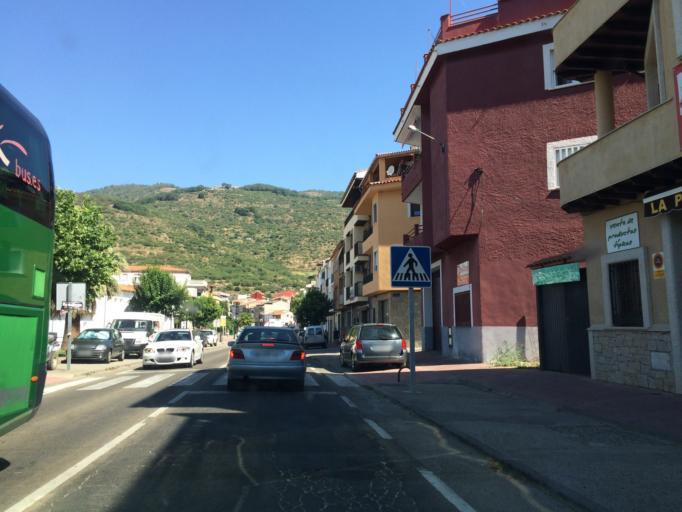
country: ES
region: Extremadura
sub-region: Provincia de Caceres
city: Cabezuela del Valle
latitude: 40.1907
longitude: -5.8062
